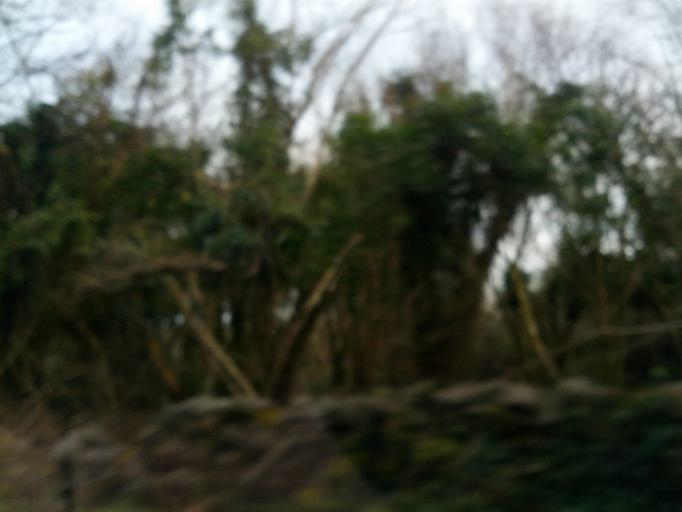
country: IE
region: Connaught
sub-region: County Galway
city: Oranmore
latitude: 53.2318
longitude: -8.8426
